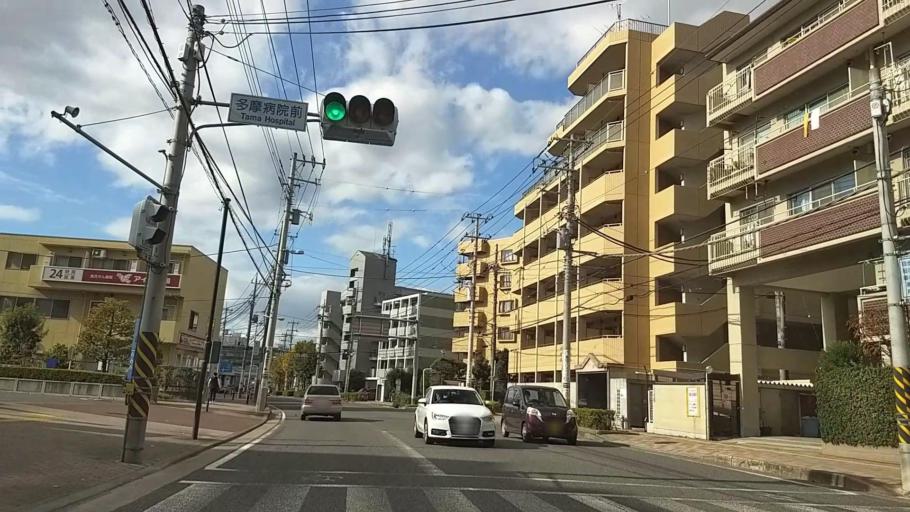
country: JP
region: Tokyo
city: Chofugaoka
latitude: 35.6204
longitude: 139.5726
